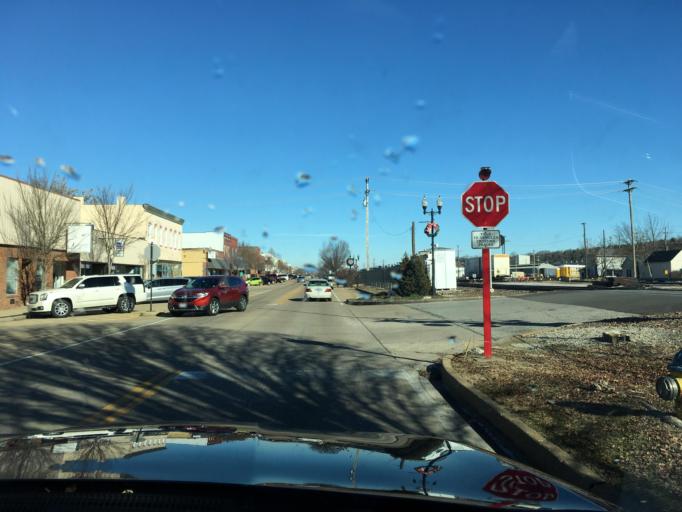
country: US
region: Missouri
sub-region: Jefferson County
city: De Soto
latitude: 38.1373
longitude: -90.5544
